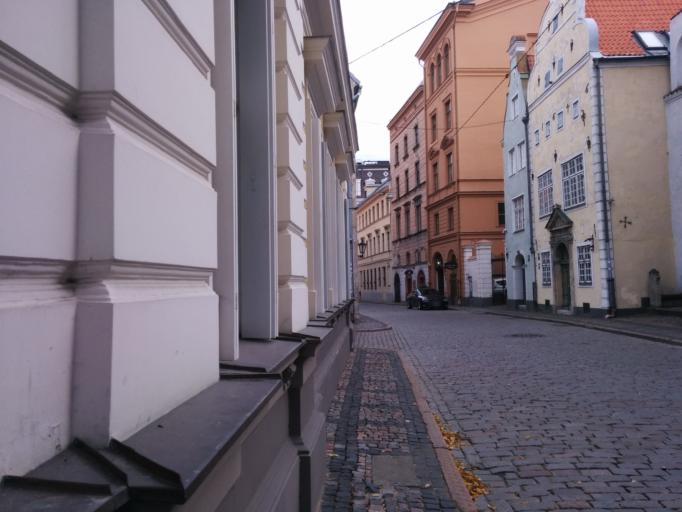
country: LV
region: Riga
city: Riga
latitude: 56.9505
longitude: 24.1039
